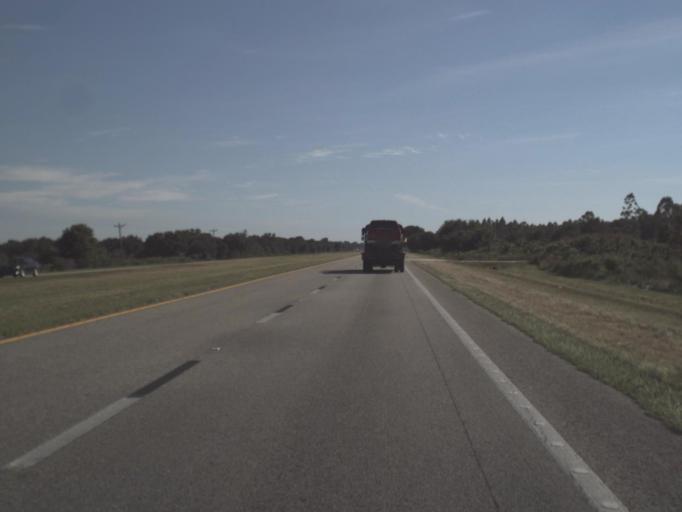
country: US
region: Florida
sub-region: Hendry County
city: Port LaBelle
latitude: 26.9969
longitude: -81.3283
